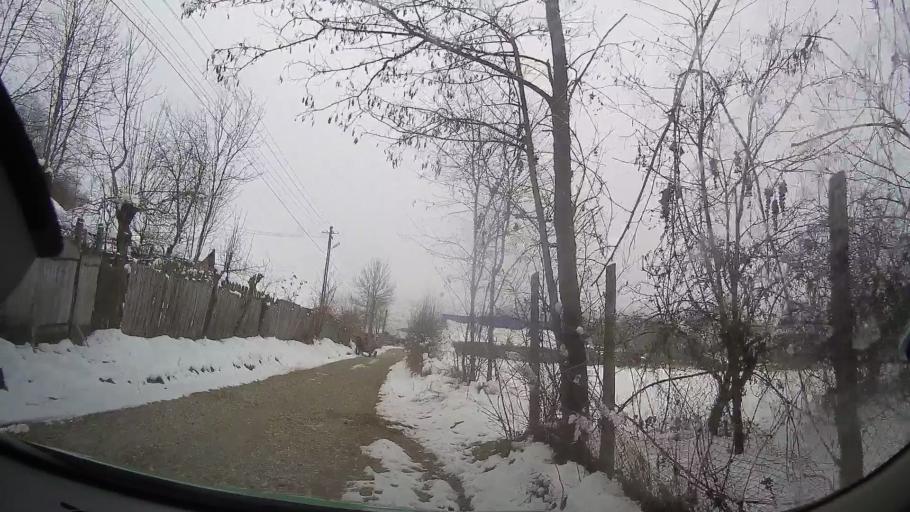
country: RO
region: Bacau
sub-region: Comuna Vultureni
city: Vultureni
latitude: 46.3716
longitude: 27.2835
